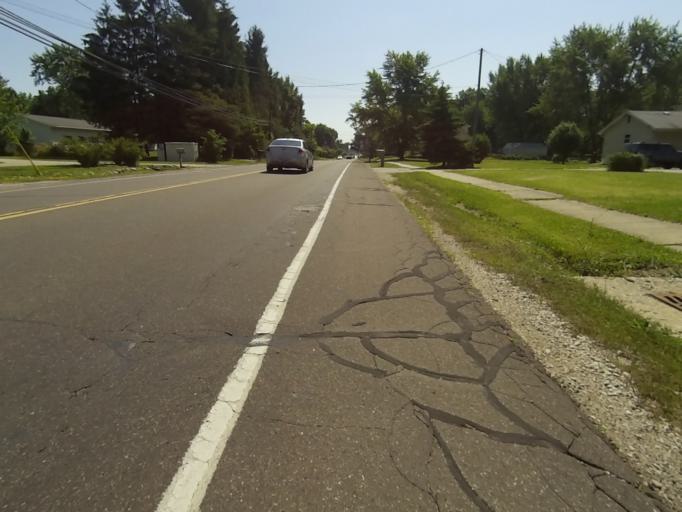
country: US
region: Ohio
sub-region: Summit County
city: Stow
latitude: 41.1667
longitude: -81.4156
